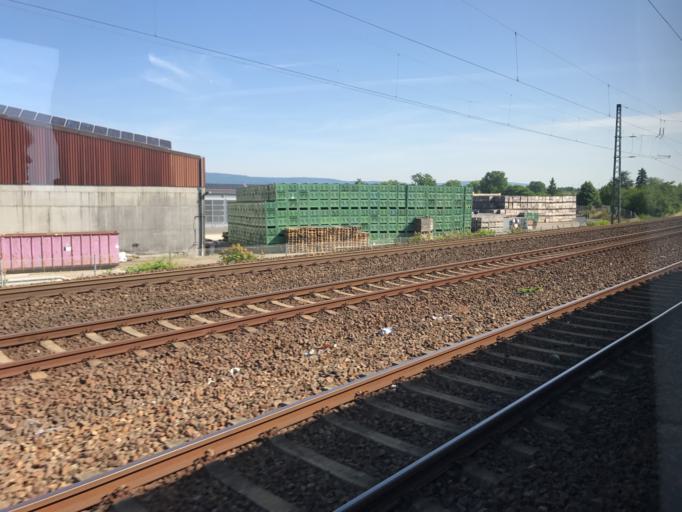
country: DE
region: Rheinland-Pfalz
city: Ingelheim am Rhein
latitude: 49.9779
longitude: 8.0574
